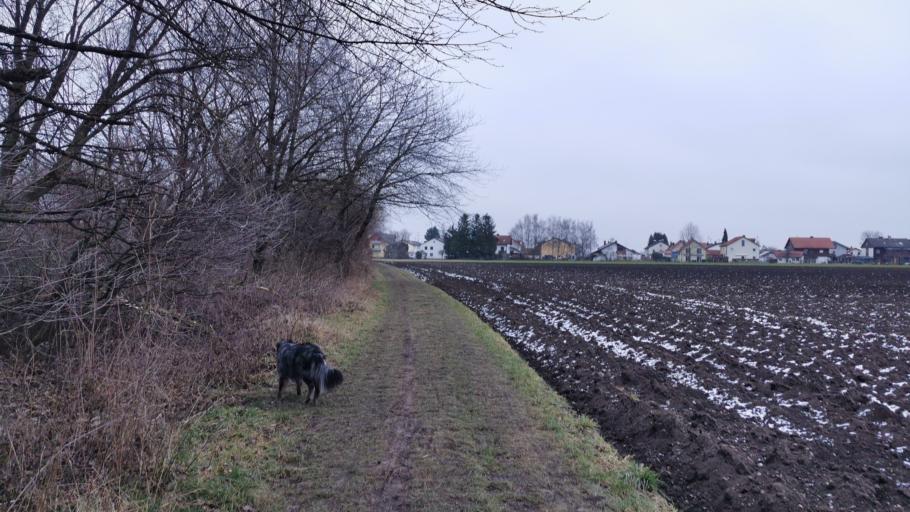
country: DE
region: Bavaria
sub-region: Upper Bavaria
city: Kirchheim bei Muenchen
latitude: 48.1974
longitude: 11.7671
